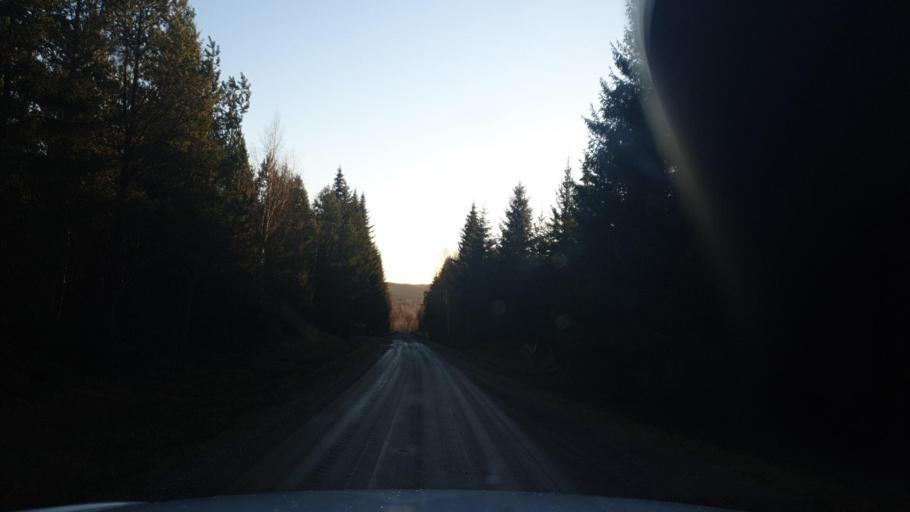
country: SE
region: Vaermland
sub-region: Eda Kommun
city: Charlottenberg
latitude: 59.9814
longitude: 12.4129
